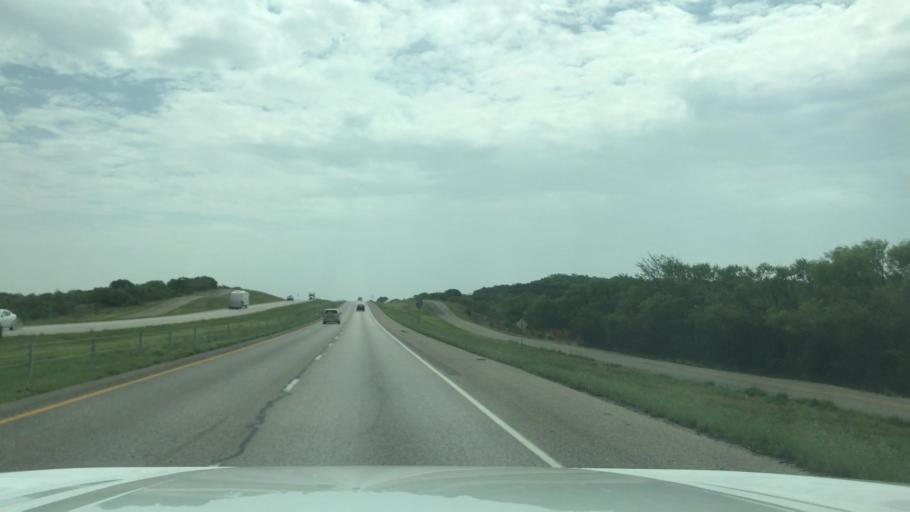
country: US
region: Texas
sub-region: Eastland County
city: Cisco
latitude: 32.3791
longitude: -99.1368
